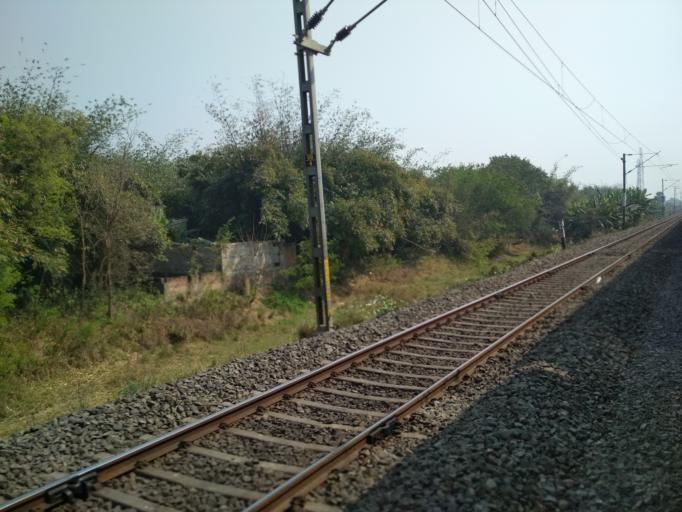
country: IN
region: Bihar
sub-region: Khagaria
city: Khagaria
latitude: 25.5082
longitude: 86.5232
